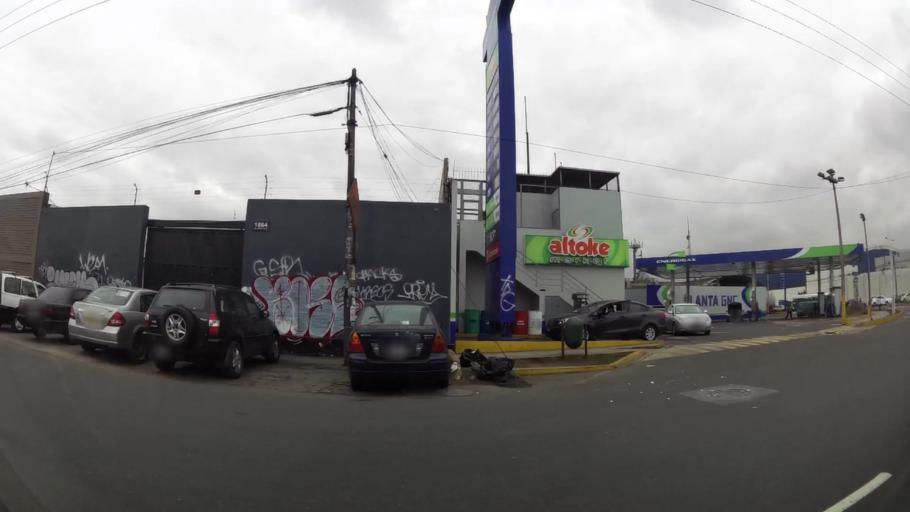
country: PE
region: Lima
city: Lima
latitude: -12.0455
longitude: -77.0659
